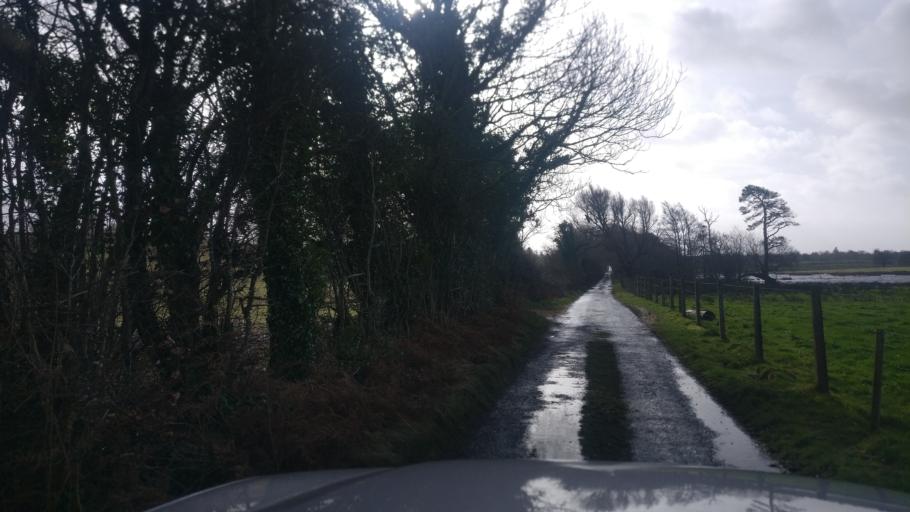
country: IE
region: Connaught
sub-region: County Galway
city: Loughrea
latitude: 53.2813
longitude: -8.5961
